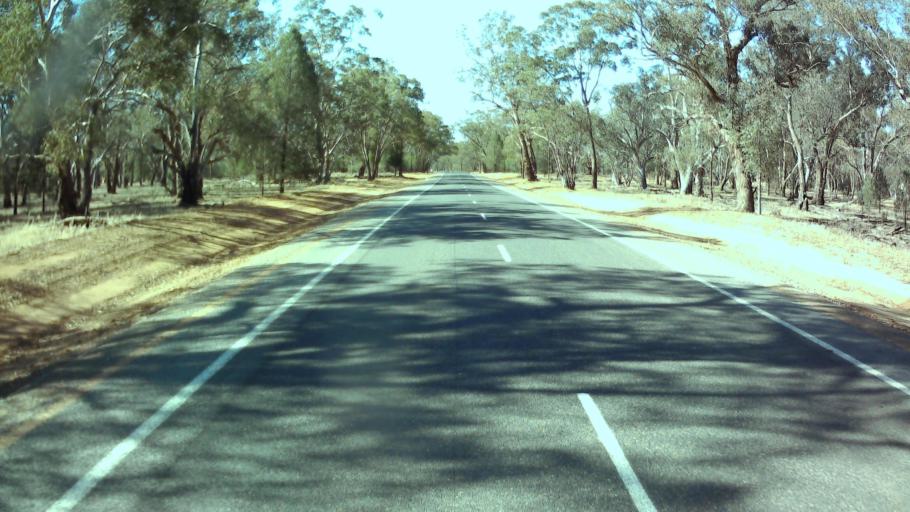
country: AU
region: New South Wales
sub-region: Weddin
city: Grenfell
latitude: -33.7622
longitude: 148.0820
